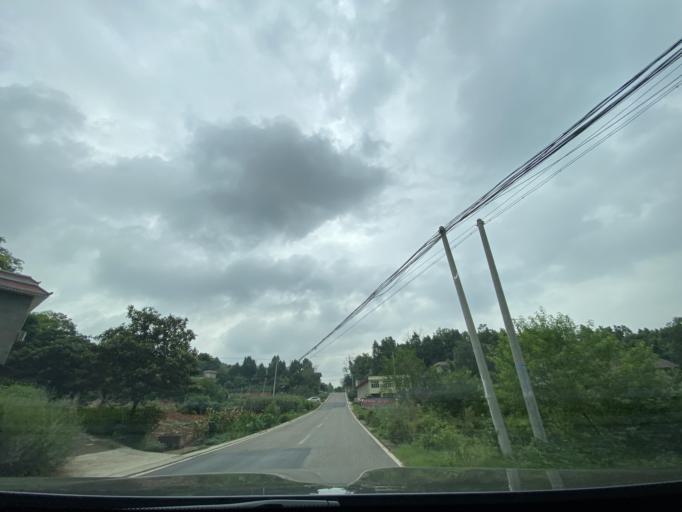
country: CN
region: Sichuan
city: Jiancheng
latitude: 30.5382
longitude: 104.5272
